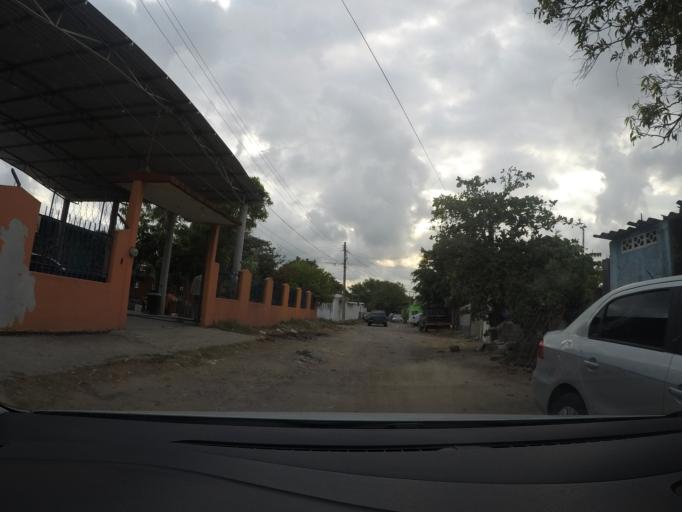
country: MX
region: Oaxaca
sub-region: Salina Cruz
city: Salina Cruz
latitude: 16.2099
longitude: -95.1987
